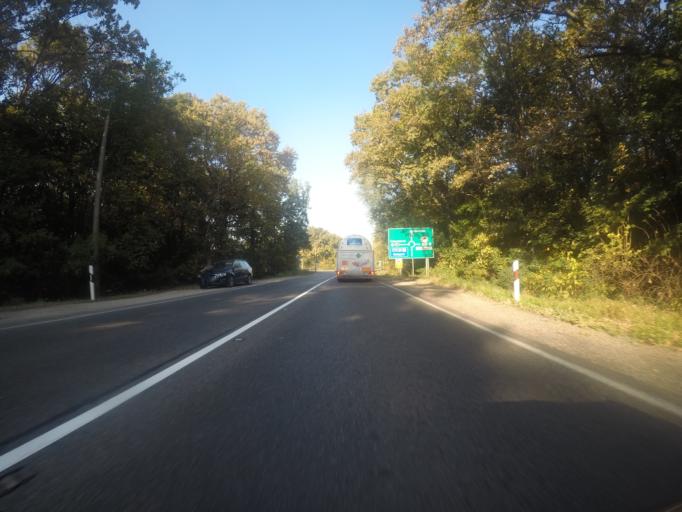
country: HU
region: Fejer
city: dunaujvaros
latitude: 46.9796
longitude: 18.9118
